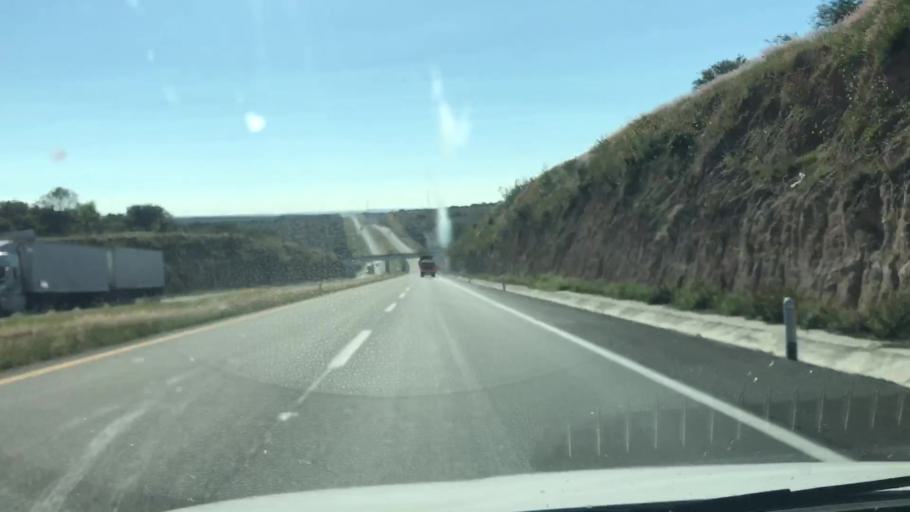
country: MX
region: Jalisco
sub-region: Union de San Antonio
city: San Jose del Caliche (El Caliche)
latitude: 21.2039
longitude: -101.9047
